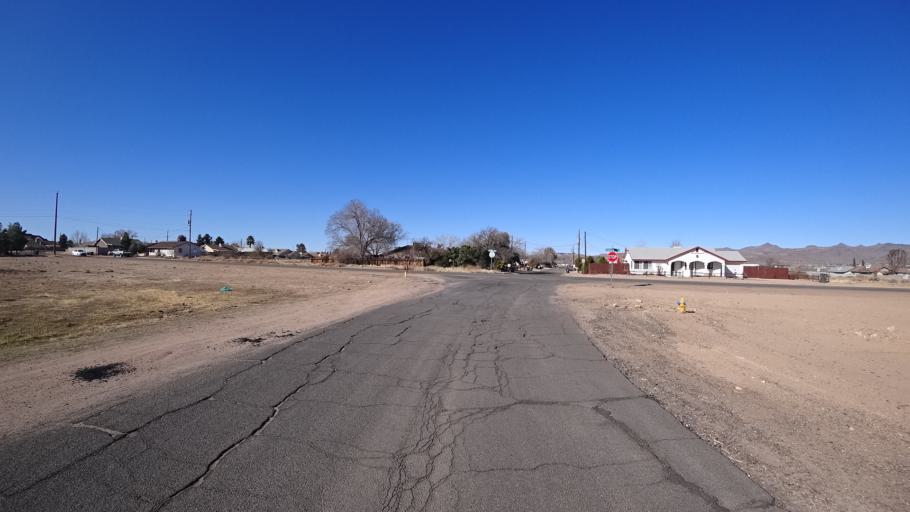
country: US
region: Arizona
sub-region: Mohave County
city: Kingman
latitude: 35.2056
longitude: -114.0111
